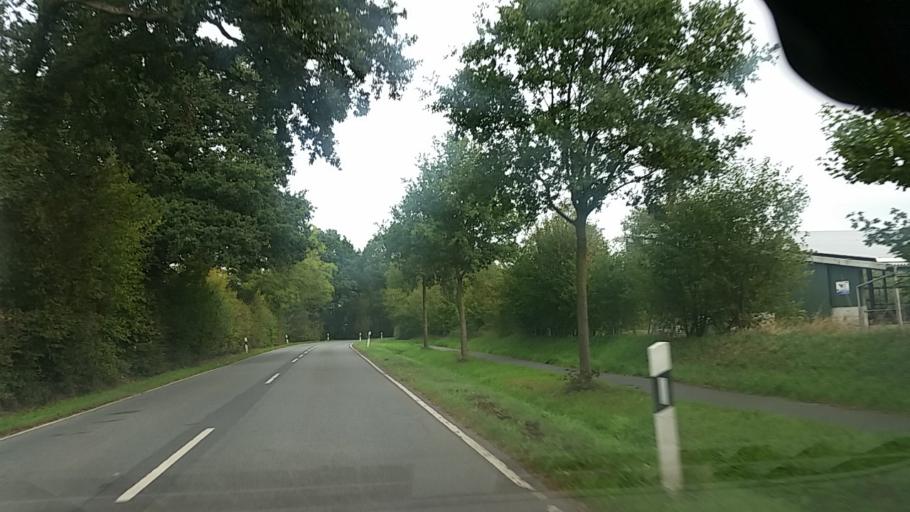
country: DE
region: Schleswig-Holstein
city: Schmalfeld
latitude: 53.8664
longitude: 9.9767
